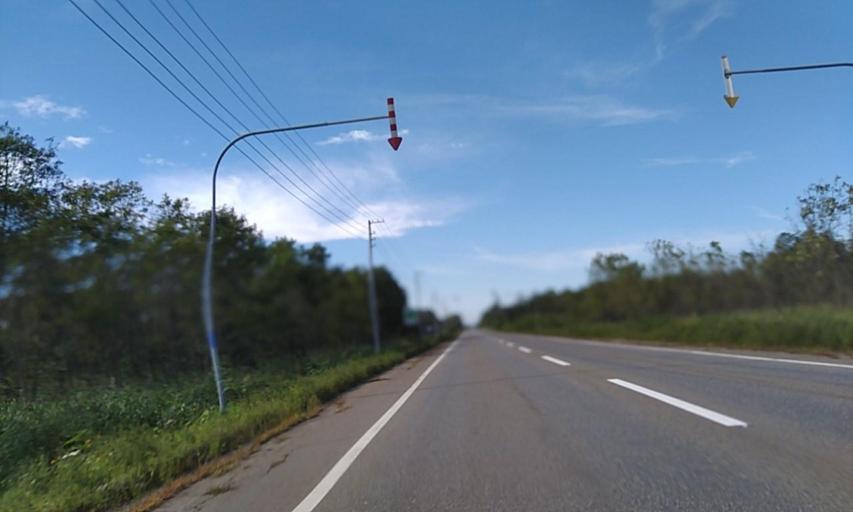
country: JP
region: Hokkaido
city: Obihiro
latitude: 42.7852
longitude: 143.5915
